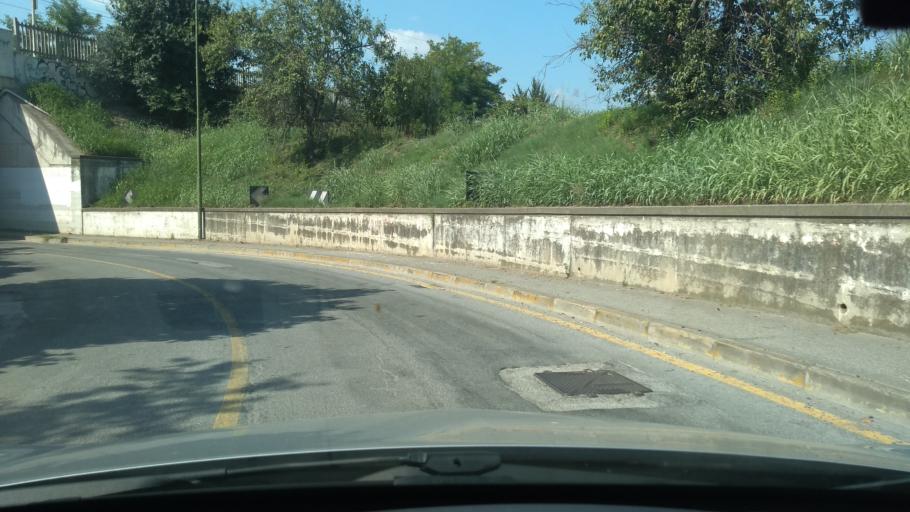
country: IT
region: Lombardy
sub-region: Provincia di Bergamo
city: Stezzano
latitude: 45.6591
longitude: 9.6455
